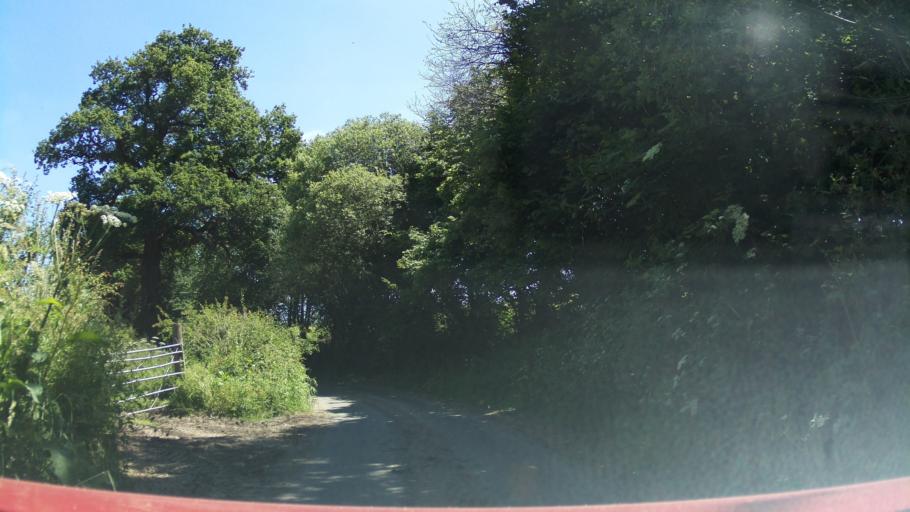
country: GB
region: England
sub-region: Wiltshire
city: Chippenham
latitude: 51.4833
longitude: -2.1133
